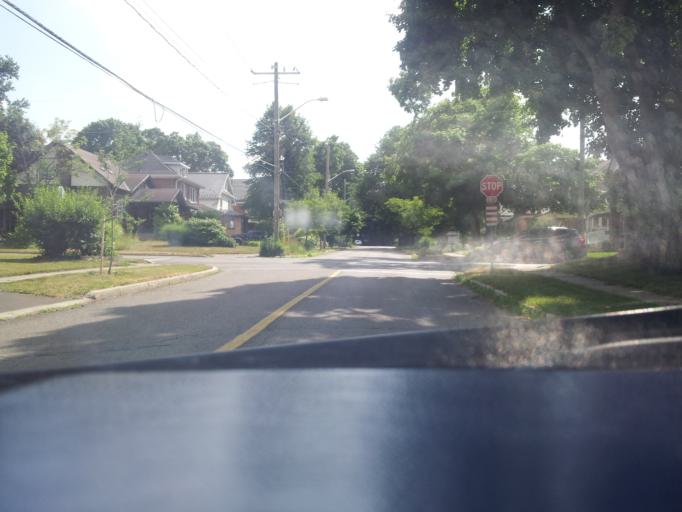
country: CA
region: Ontario
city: Waterloo
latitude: 43.4565
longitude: -80.5233
